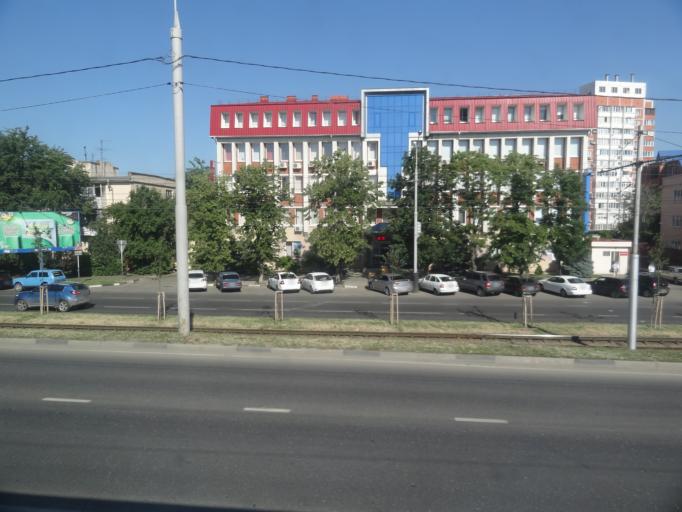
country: RU
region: Adygeya
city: Yablonovskiy
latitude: 45.0035
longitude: 38.9655
